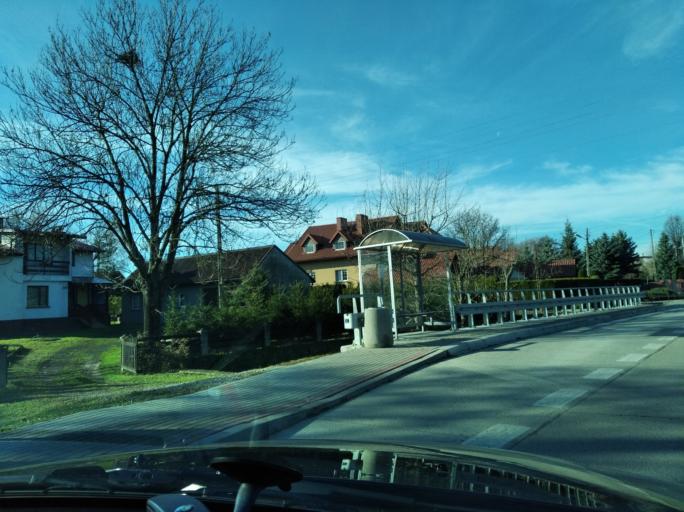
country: PL
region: Subcarpathian Voivodeship
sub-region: Powiat rzeszowski
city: Kielanowka
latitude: 50.0100
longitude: 21.9387
